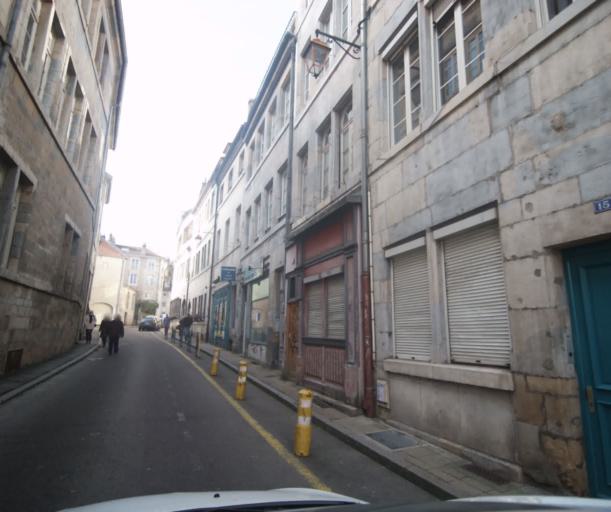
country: FR
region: Franche-Comte
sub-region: Departement du Doubs
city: Besancon
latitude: 47.2352
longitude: 6.0313
